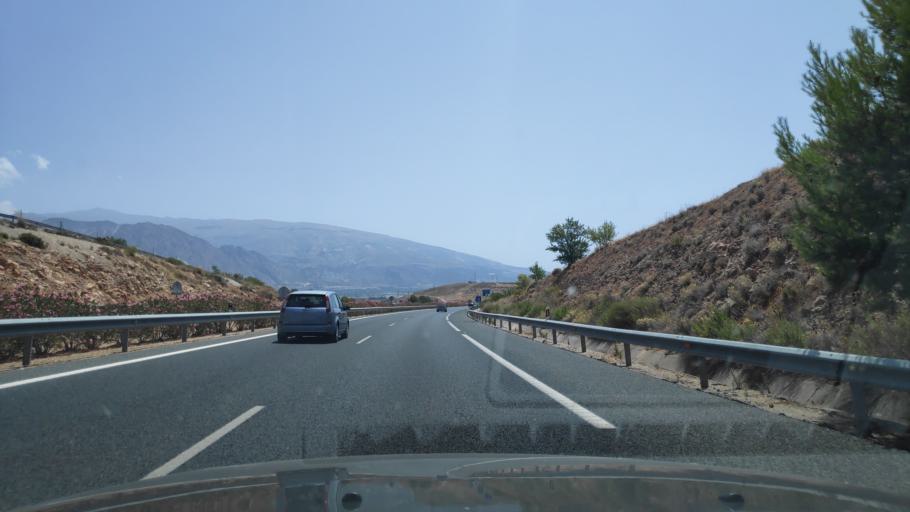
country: ES
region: Andalusia
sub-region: Provincia de Granada
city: Padul
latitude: 36.9907
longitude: -3.6153
